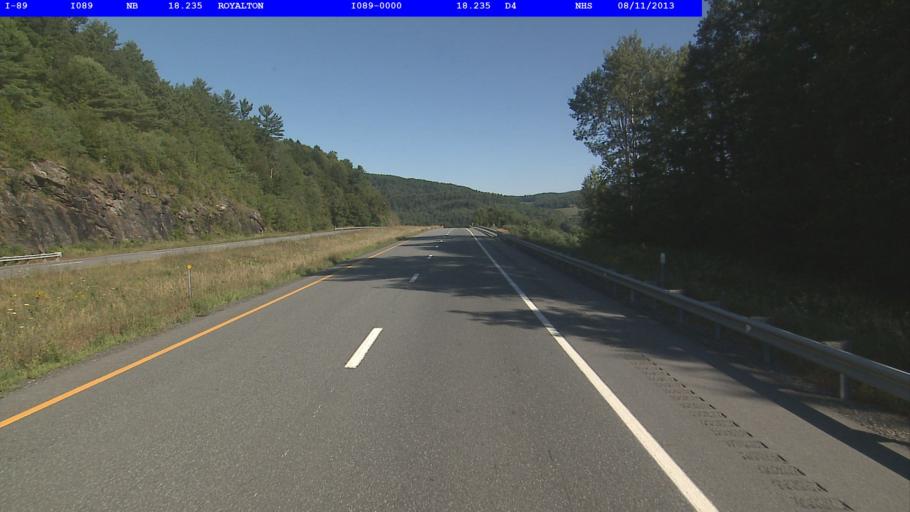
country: US
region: Vermont
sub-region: Orange County
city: Randolph
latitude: 43.8171
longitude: -72.5244
